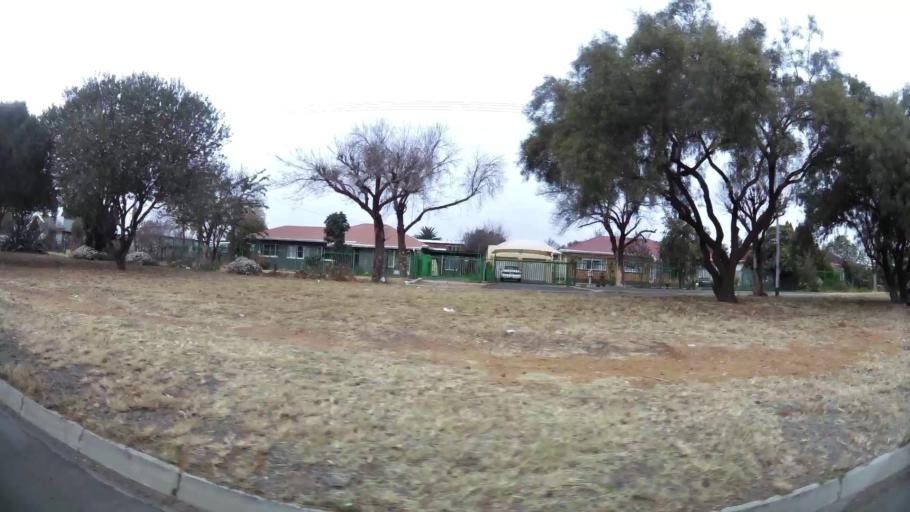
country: ZA
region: Orange Free State
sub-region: Mangaung Metropolitan Municipality
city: Bloemfontein
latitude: -29.1268
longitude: 26.1708
